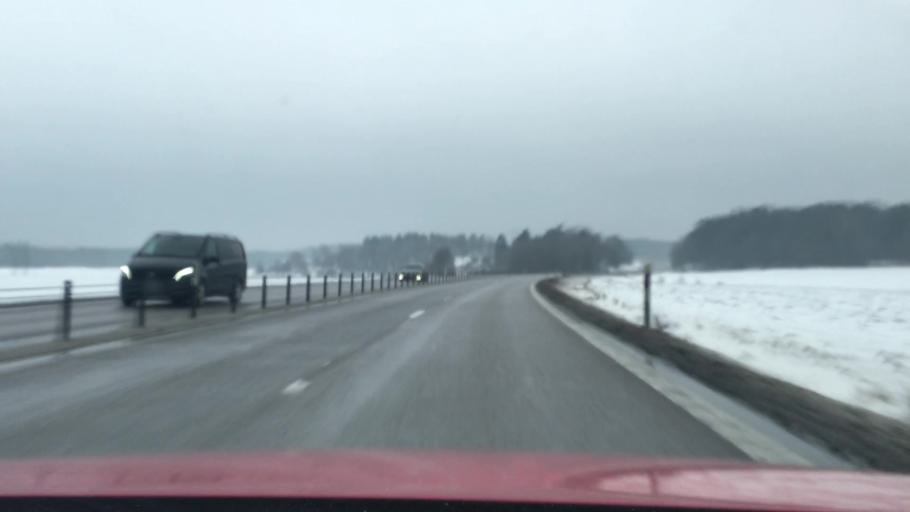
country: SE
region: Vaestra Goetaland
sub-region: Vanersborgs Kommun
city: Vanersborg
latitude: 58.3475
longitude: 12.3124
